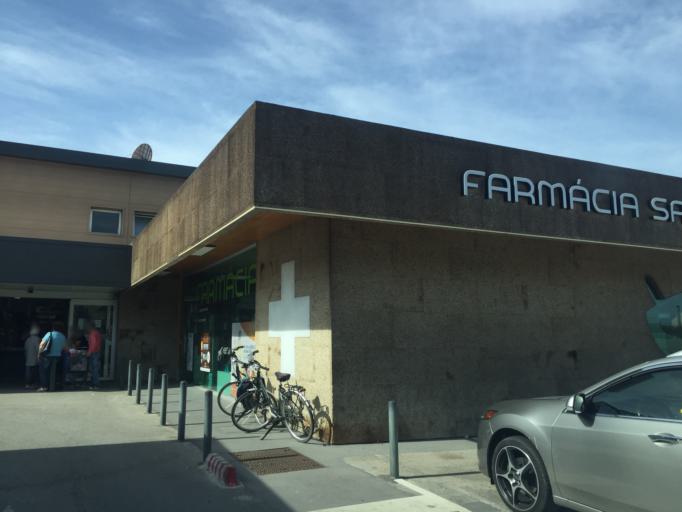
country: PT
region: Coimbra
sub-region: Figueira da Foz
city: Lavos
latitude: 40.0852
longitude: -8.8250
